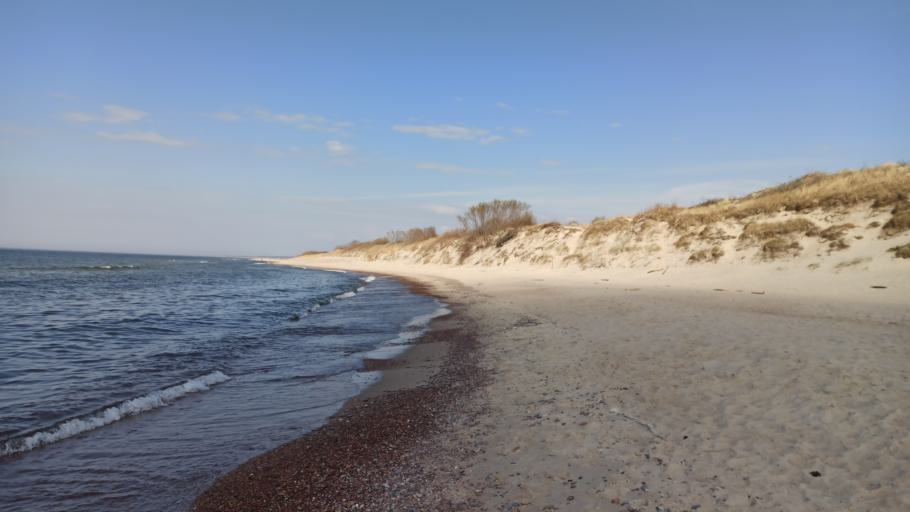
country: LT
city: Nida
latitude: 55.2242
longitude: 20.8901
